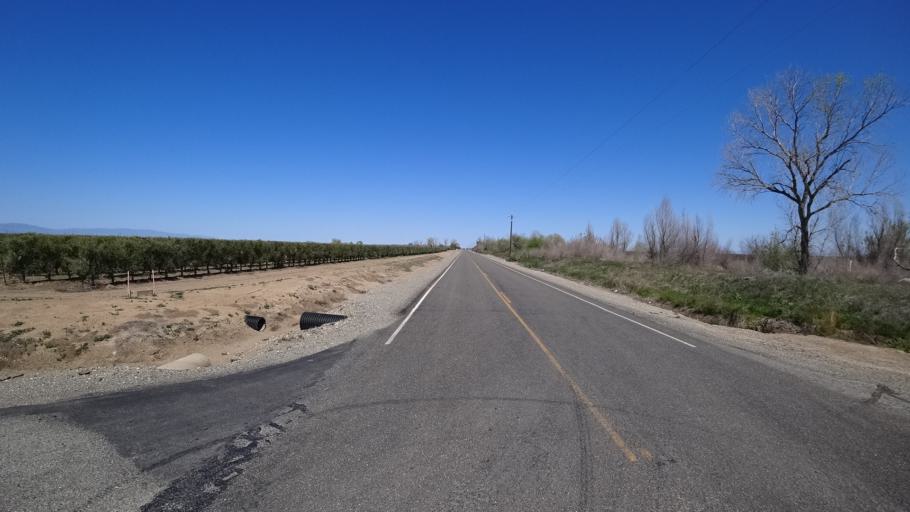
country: US
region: California
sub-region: Glenn County
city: Willows
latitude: 39.6117
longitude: -122.2500
